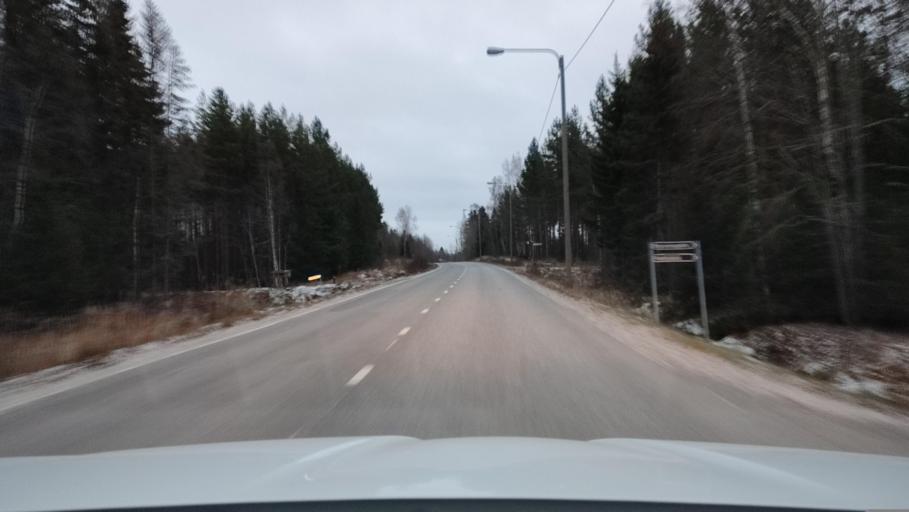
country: FI
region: Ostrobothnia
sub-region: Vaasa
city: Replot
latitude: 63.2359
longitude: 21.3982
